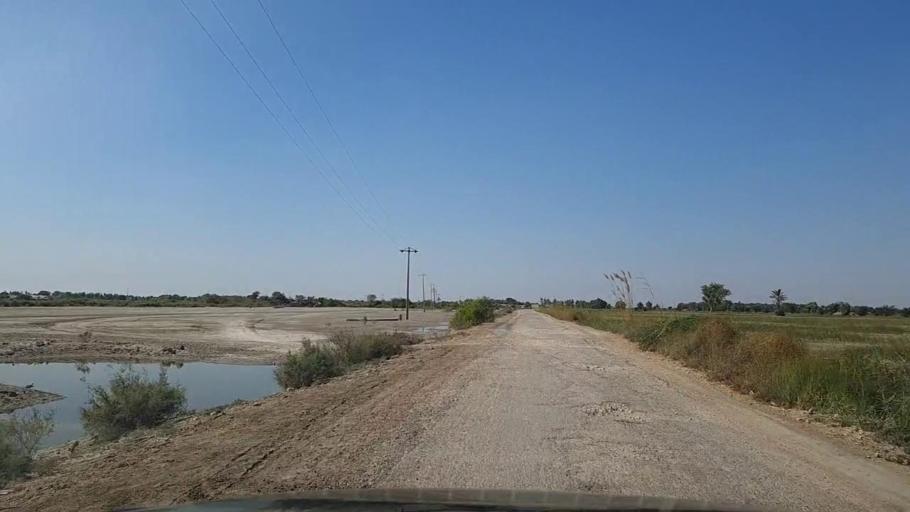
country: PK
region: Sindh
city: Mirpur Sakro
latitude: 24.6088
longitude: 67.7848
